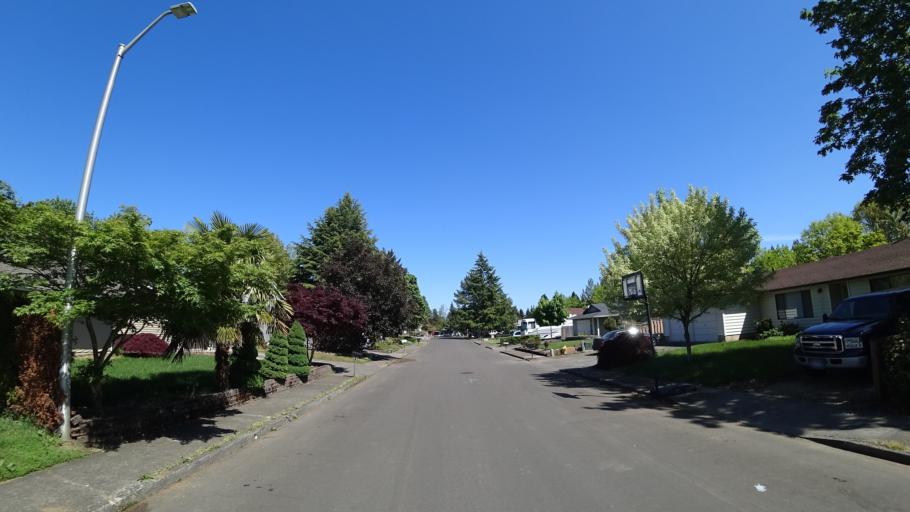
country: US
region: Oregon
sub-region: Washington County
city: Hillsboro
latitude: 45.5094
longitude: -122.9596
